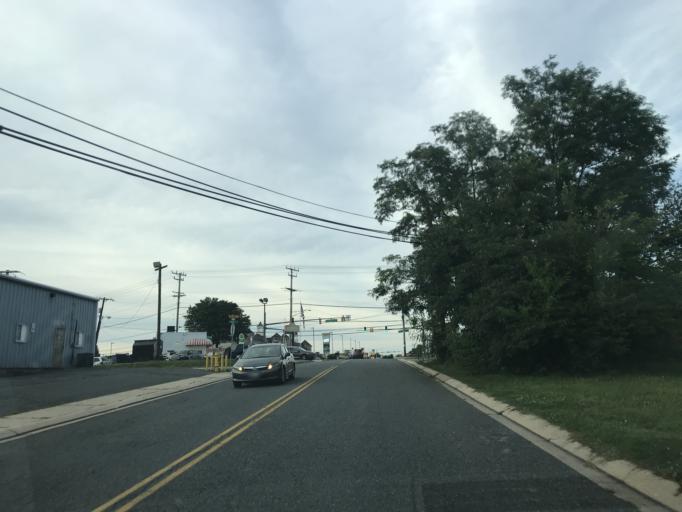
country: US
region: Maryland
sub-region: Harford County
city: Aberdeen
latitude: 39.5186
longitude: -76.1861
